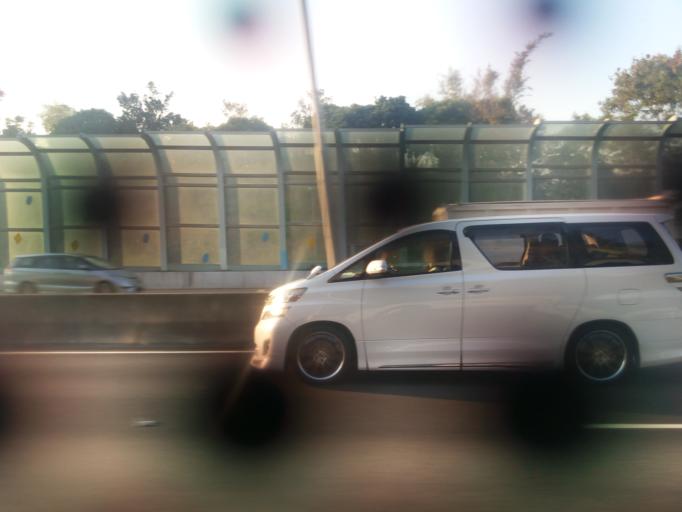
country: HK
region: Yuen Long
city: Yuen Long Kau Hui
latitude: 22.4260
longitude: 113.9997
